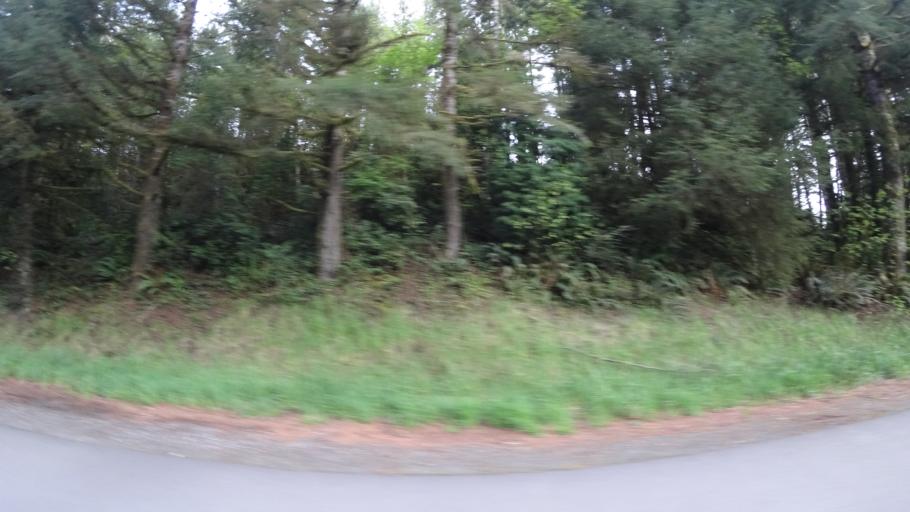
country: US
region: Oregon
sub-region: Coos County
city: Barview
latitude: 43.2541
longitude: -124.2854
